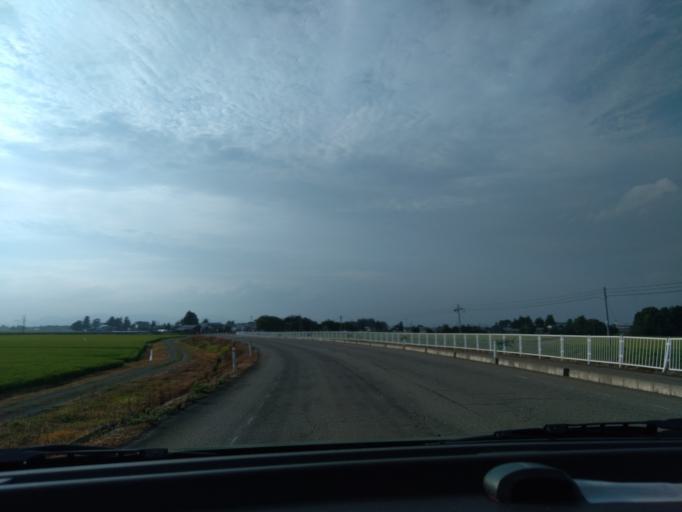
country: JP
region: Akita
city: Yokotemachi
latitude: 39.3794
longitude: 140.5324
